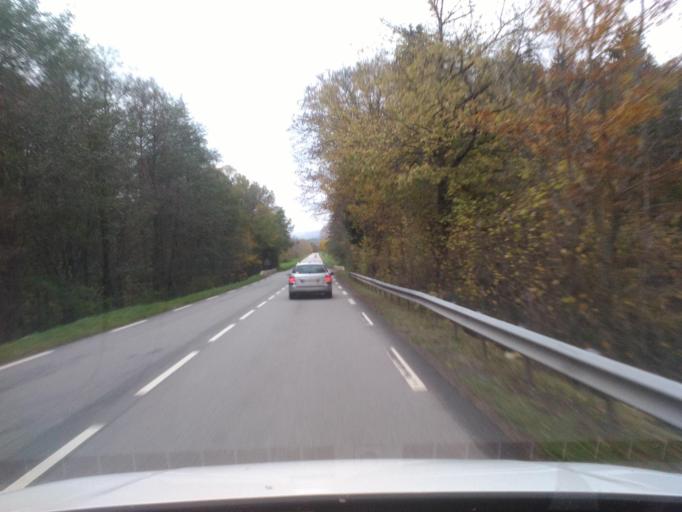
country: FR
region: Lorraine
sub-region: Departement des Vosges
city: Ban-de-Laveline
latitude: 48.3200
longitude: 7.0940
